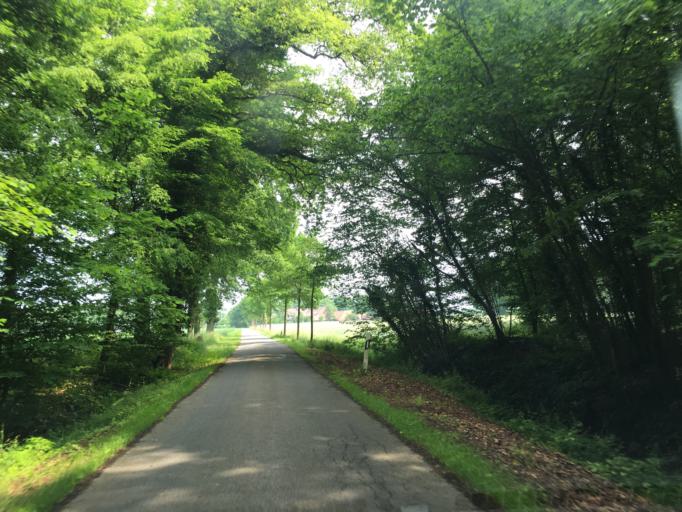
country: DE
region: North Rhine-Westphalia
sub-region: Regierungsbezirk Munster
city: Greven
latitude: 52.0407
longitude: 7.5872
